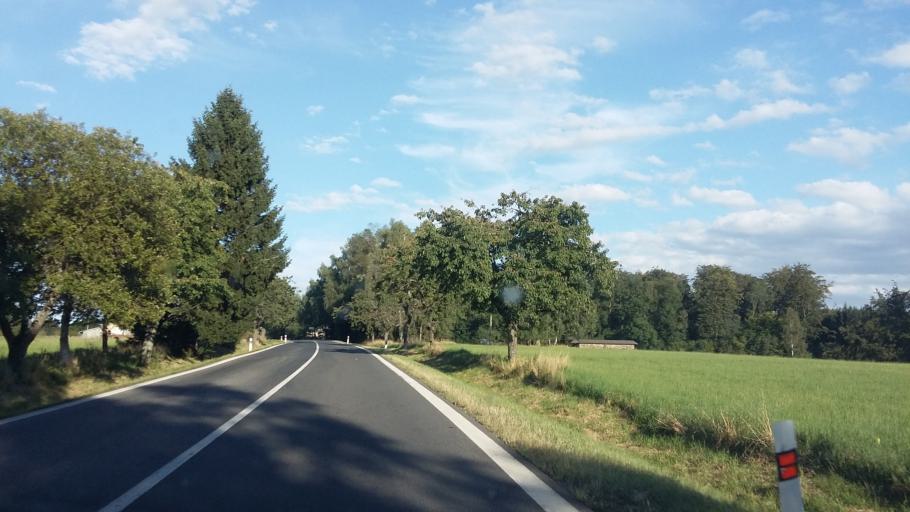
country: CZ
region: Plzensky
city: Strasice
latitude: 49.6230
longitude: 13.7511
